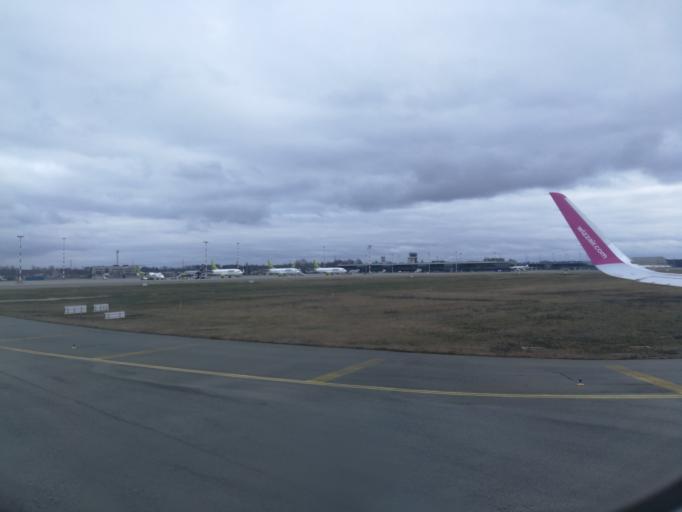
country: LV
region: Babite
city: Pinki
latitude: 56.9296
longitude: 23.9727
